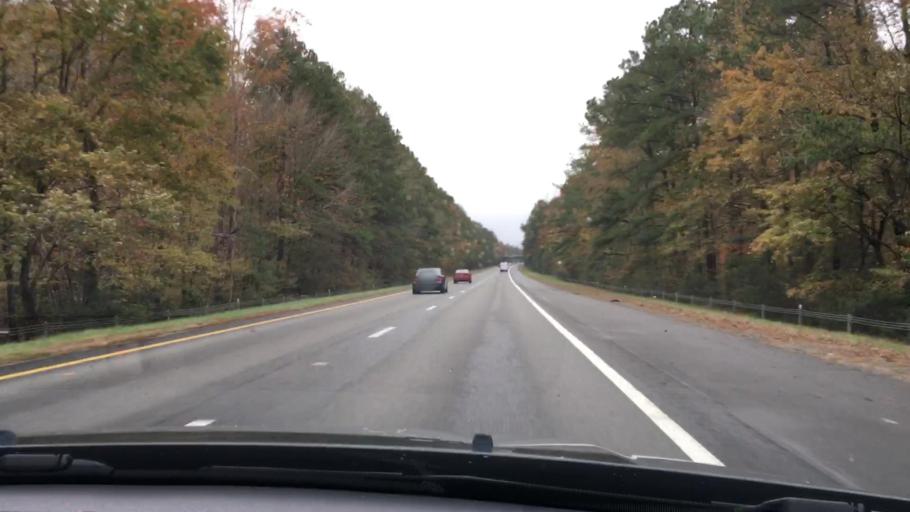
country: US
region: Virginia
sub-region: King William County
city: West Point
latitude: 37.4526
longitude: -76.8714
